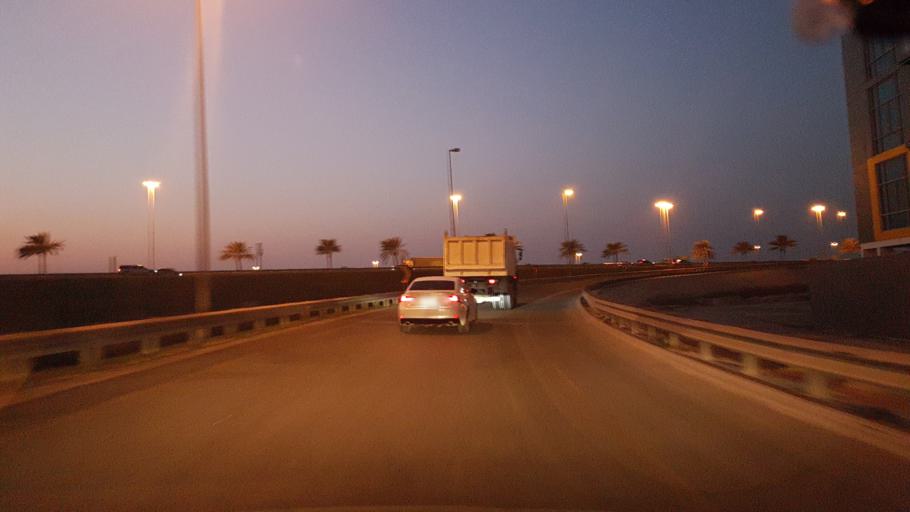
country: BH
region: Northern
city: Madinat `Isa
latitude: 26.1884
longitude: 50.5054
